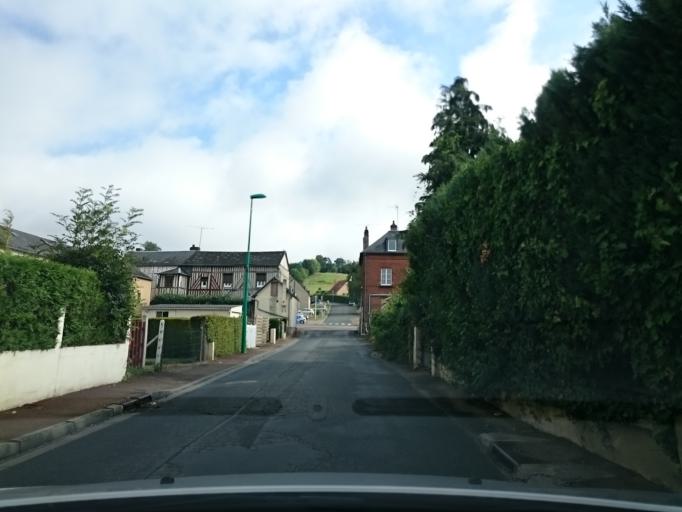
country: FR
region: Lower Normandy
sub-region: Departement du Calvados
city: Beuvillers
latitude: 49.1303
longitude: 0.2577
